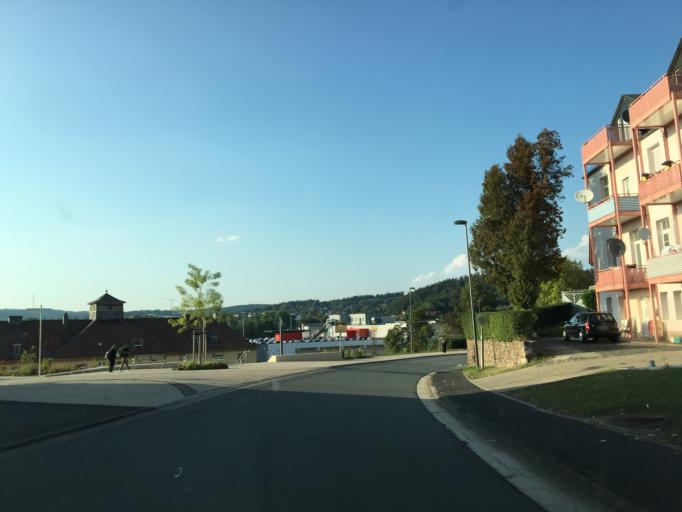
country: DE
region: Hesse
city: Frankenberg
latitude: 51.0537
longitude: 8.7905
